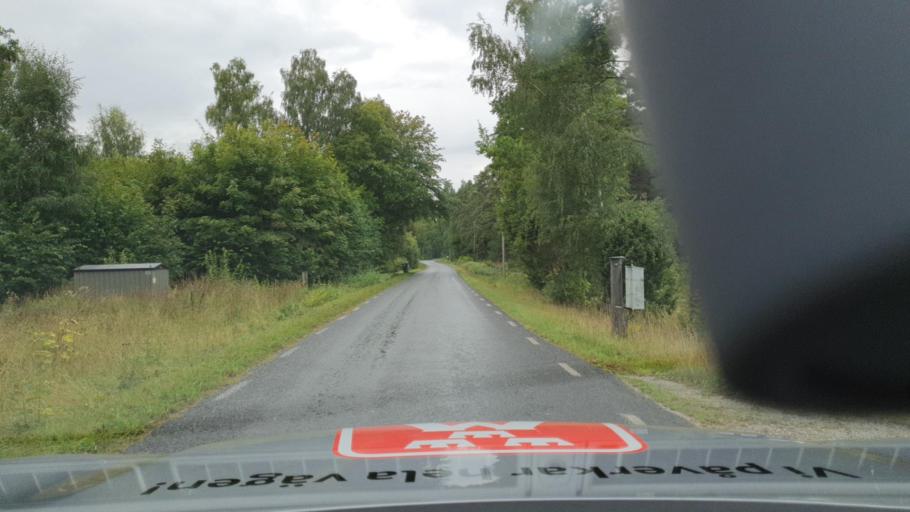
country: SE
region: Gotland
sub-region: Gotland
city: Visby
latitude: 57.5683
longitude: 18.5186
